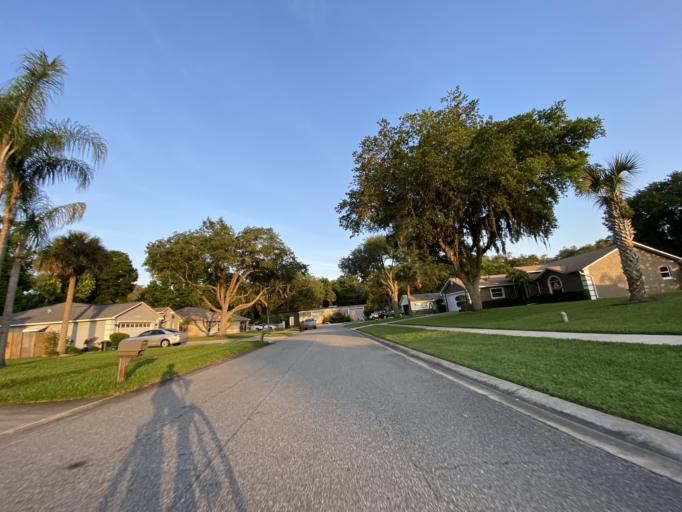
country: US
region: Florida
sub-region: Volusia County
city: Port Orange
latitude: 29.1432
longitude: -81.0049
